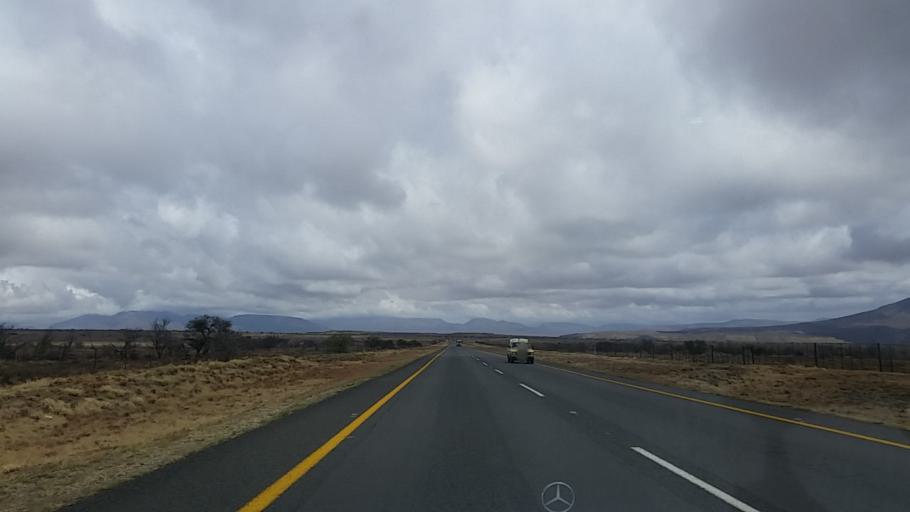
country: ZA
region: Eastern Cape
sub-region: Cacadu District Municipality
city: Graaff-Reinet
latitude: -32.1257
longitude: 24.5958
